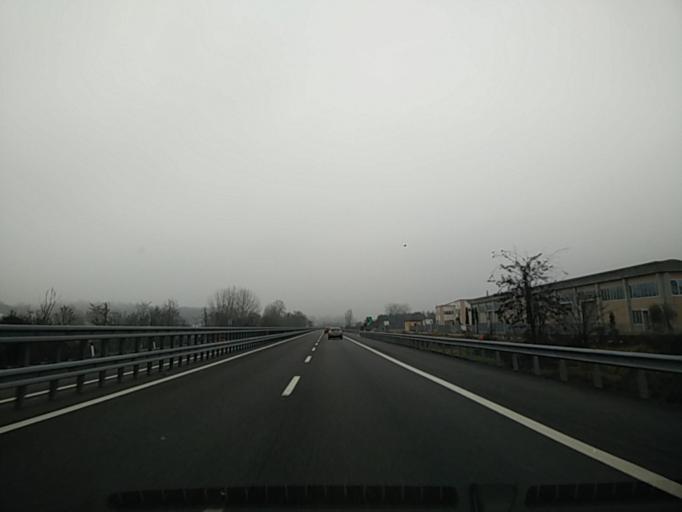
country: IT
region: Piedmont
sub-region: Provincia di Asti
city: Villafranca d'Asti
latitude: 44.9138
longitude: 8.0397
